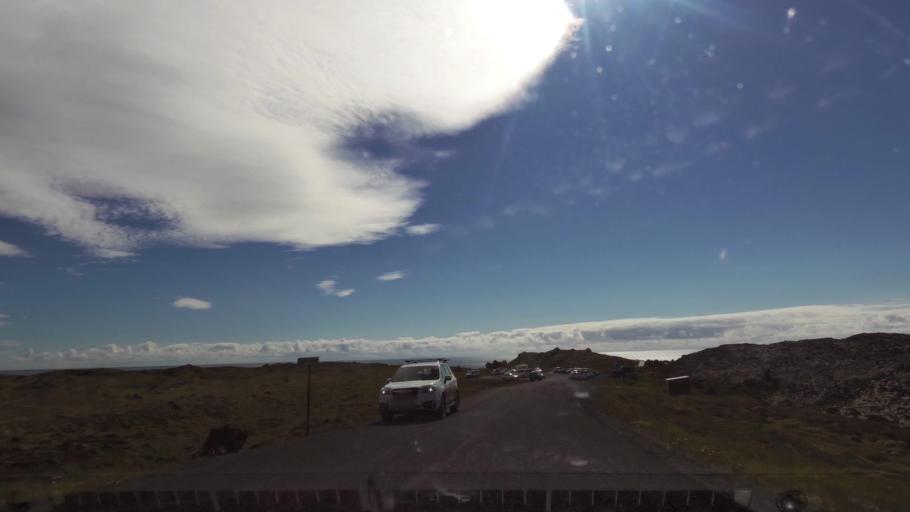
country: IS
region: West
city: Olafsvik
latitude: 64.7541
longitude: -23.8928
